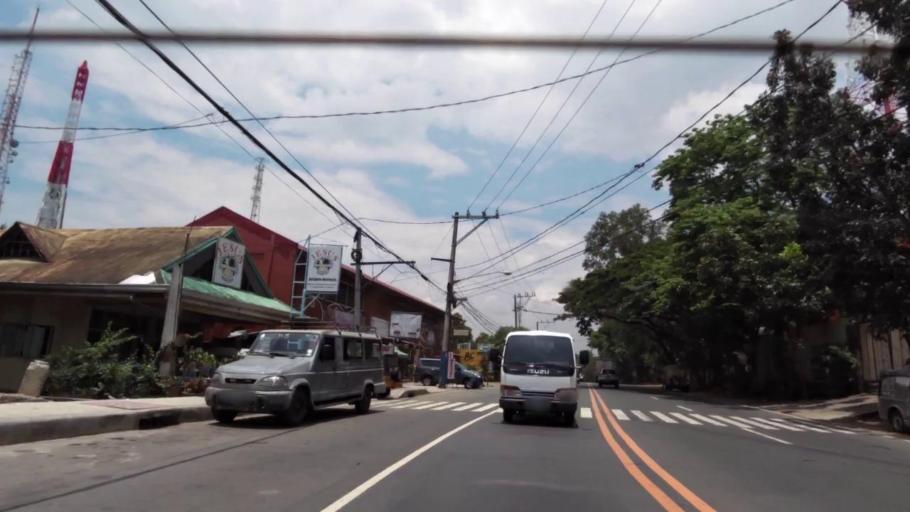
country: PH
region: Calabarzon
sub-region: Province of Rizal
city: Antipolo
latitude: 14.6073
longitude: 121.1652
